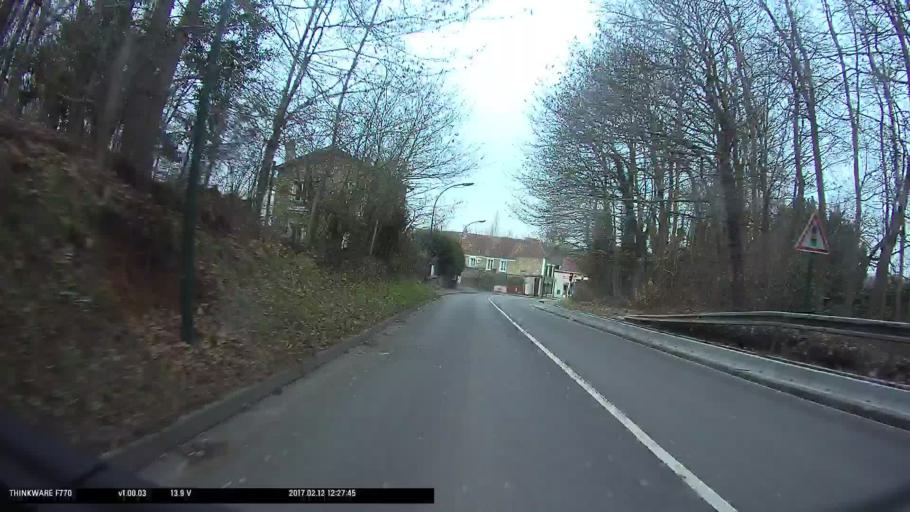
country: FR
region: Ile-de-France
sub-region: Departement du Val-d'Oise
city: Courdimanche
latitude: 49.0232
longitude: 1.9996
